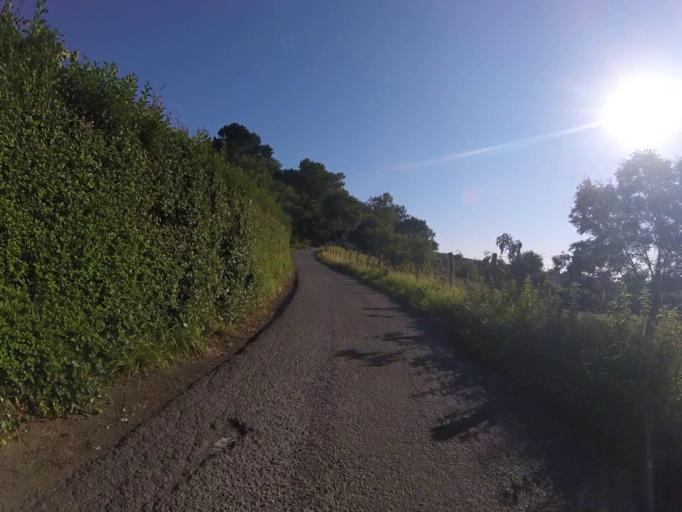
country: ES
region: Basque Country
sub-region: Provincia de Guipuzcoa
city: Fuenterrabia
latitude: 43.3786
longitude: -1.8076
